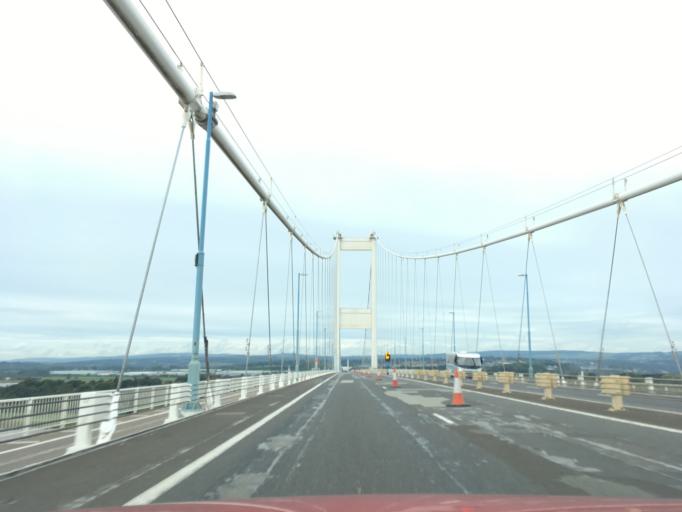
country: GB
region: Wales
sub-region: Monmouthshire
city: Chepstow
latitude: 51.6102
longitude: -2.6412
